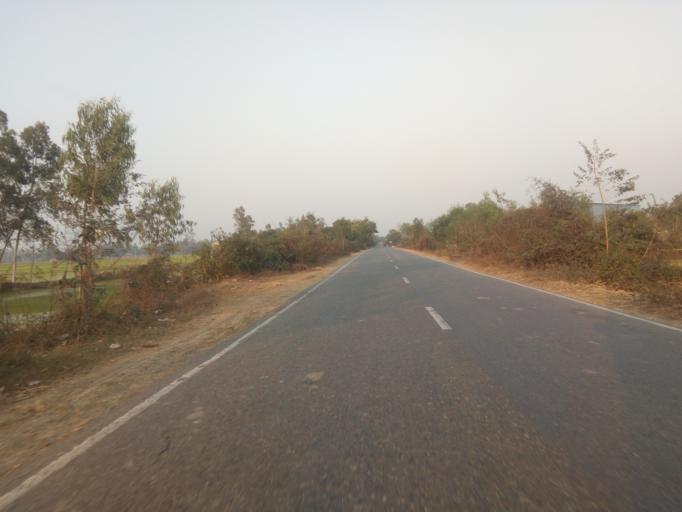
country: BD
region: Rajshahi
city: Bogra
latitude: 24.5861
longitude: 89.2302
